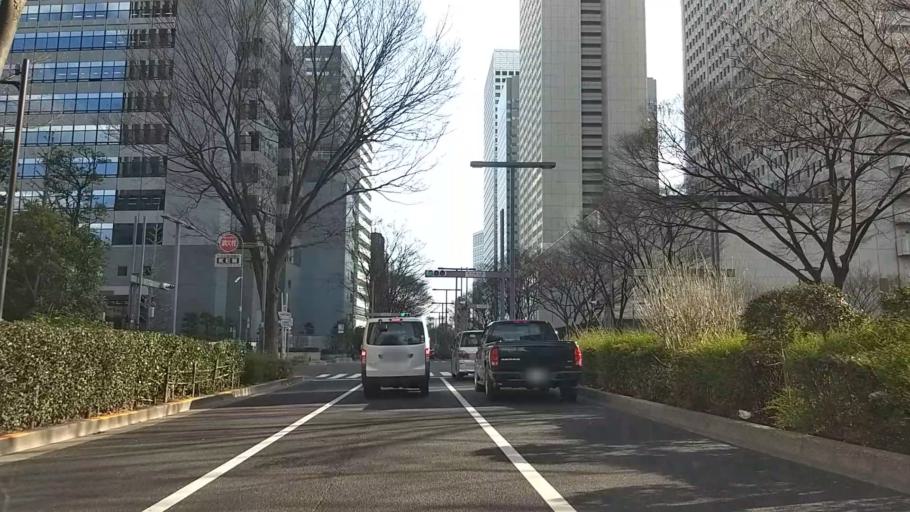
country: JP
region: Tokyo
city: Tokyo
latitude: 35.6916
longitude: 139.6947
